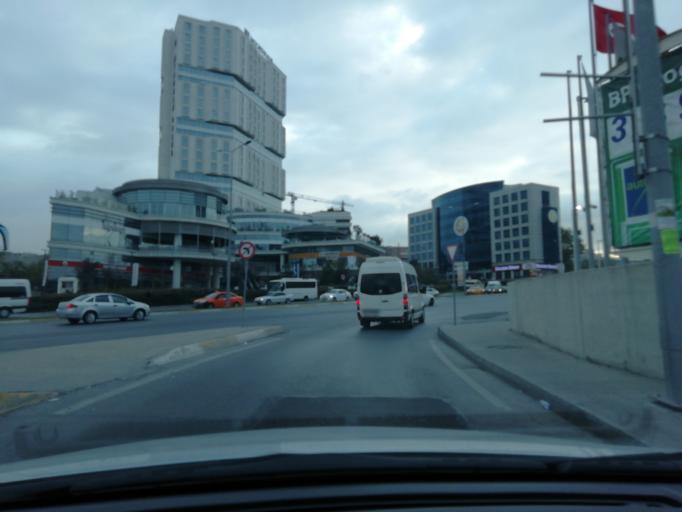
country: TR
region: Istanbul
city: Mahmutbey
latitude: 41.0263
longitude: 28.8136
